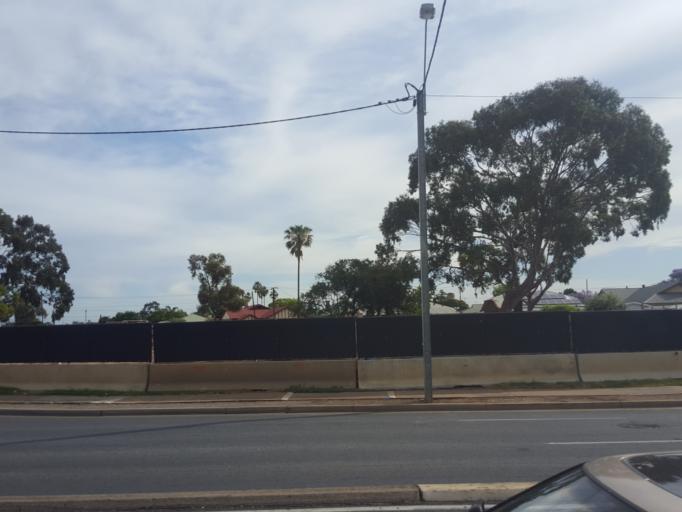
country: AU
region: South Australia
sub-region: Charles Sturt
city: Allenby Gardens
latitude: -34.8882
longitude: 138.5699
